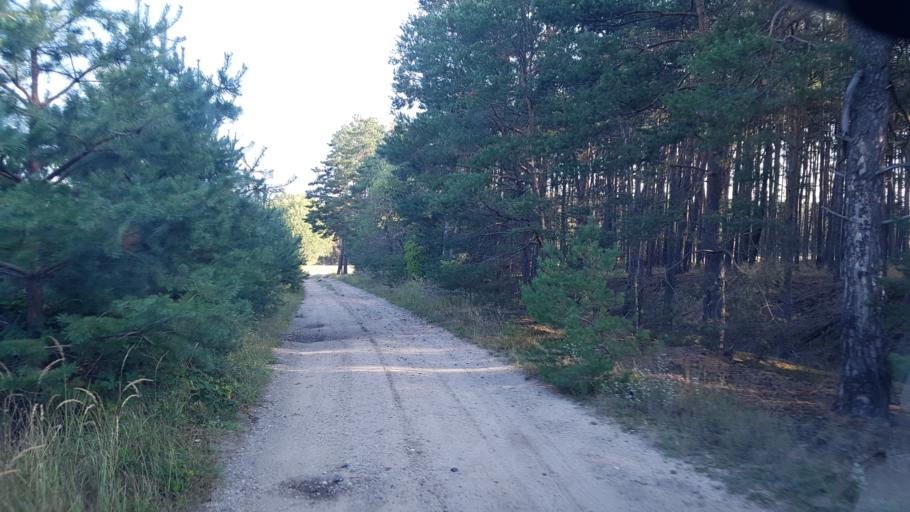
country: DE
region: Brandenburg
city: Sonnewalde
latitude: 51.6483
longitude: 13.6487
